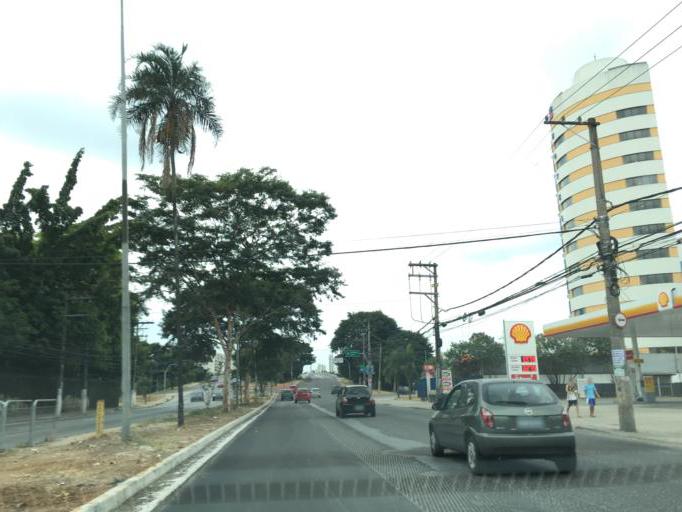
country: BR
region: Sao Paulo
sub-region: Osasco
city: Osasco
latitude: -23.5481
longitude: -46.7370
